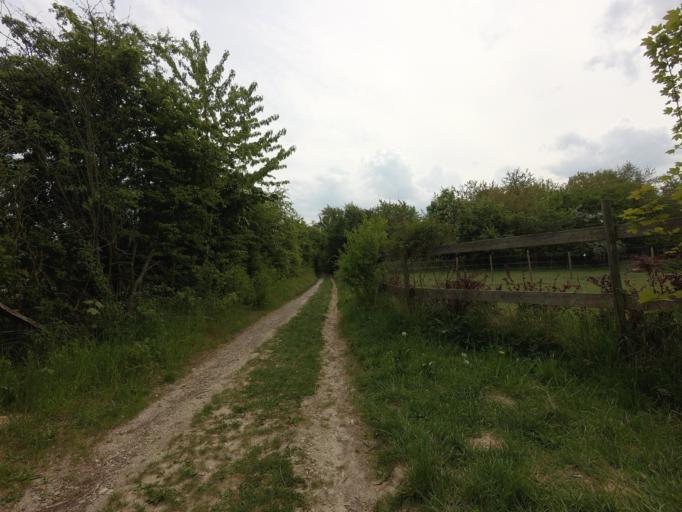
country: DE
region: Lower Saxony
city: Diekholzen
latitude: 52.1336
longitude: 9.9082
